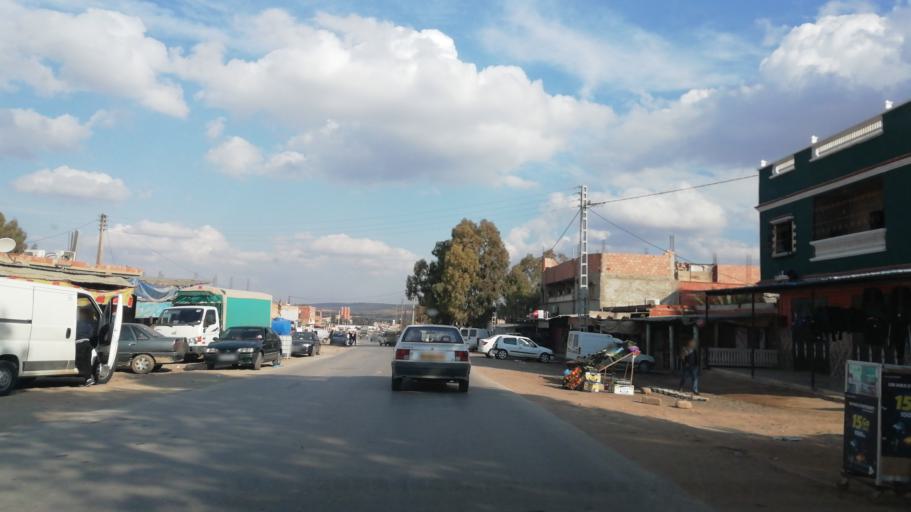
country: DZ
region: Mostaganem
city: Mostaganem
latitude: 35.8966
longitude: 0.2582
